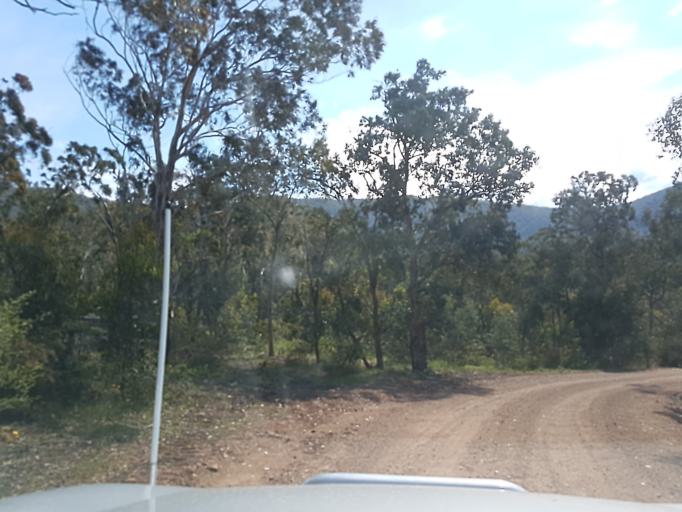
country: AU
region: Victoria
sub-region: Alpine
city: Mount Beauty
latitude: -37.3739
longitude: 147.0444
